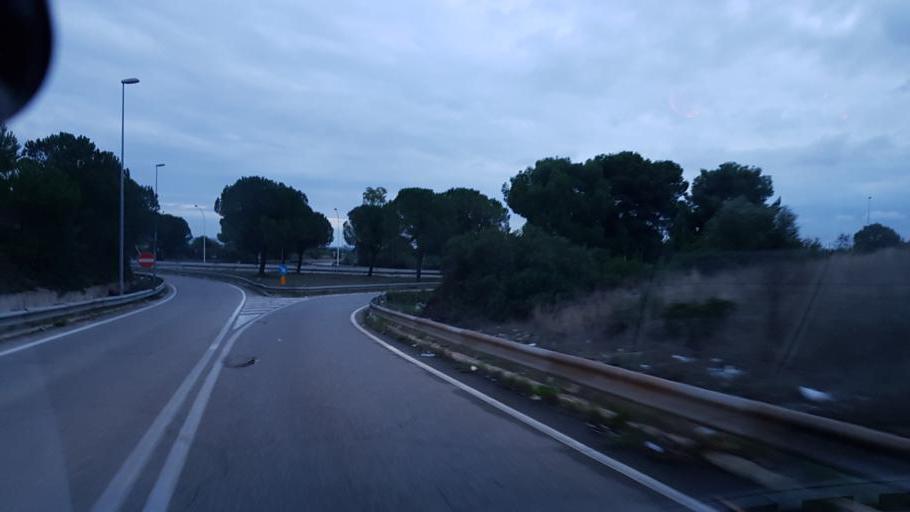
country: IT
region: Apulia
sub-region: Provincia di Taranto
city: Paolo VI
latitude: 40.5130
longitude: 17.2905
